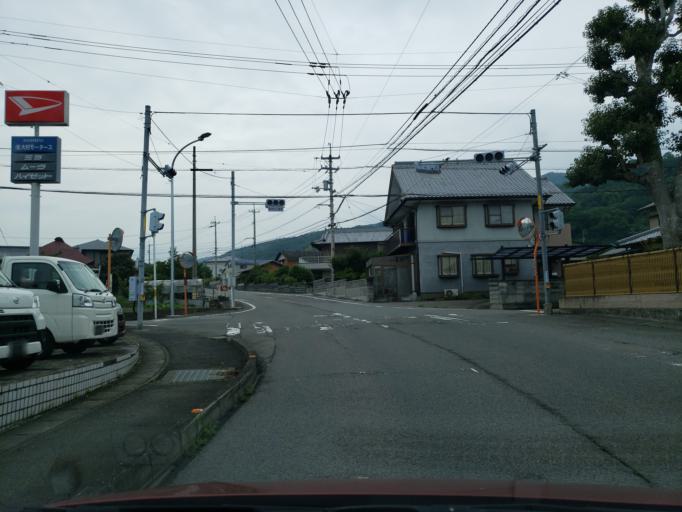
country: JP
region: Tokushima
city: Kamojimacho-jogejima
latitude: 34.1047
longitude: 134.2650
